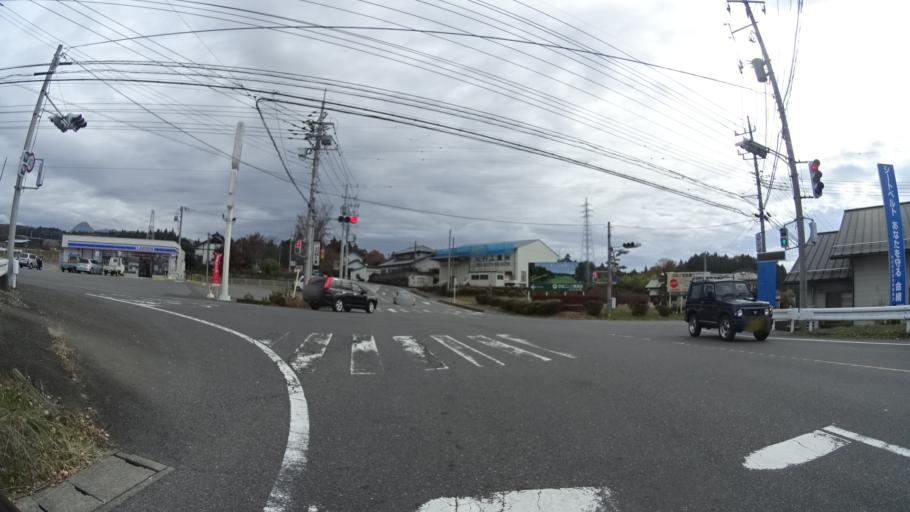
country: JP
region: Gunma
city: Shibukawa
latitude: 36.5319
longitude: 139.0566
